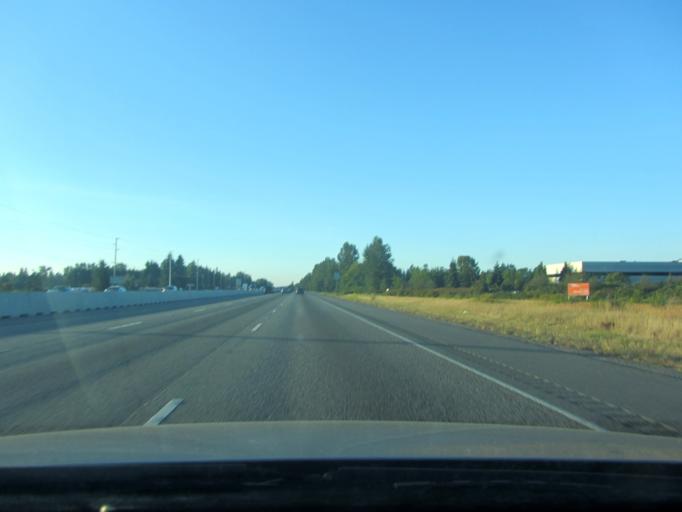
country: US
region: Washington
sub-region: Snohomish County
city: Smokey Point
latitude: 48.1087
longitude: -122.1847
